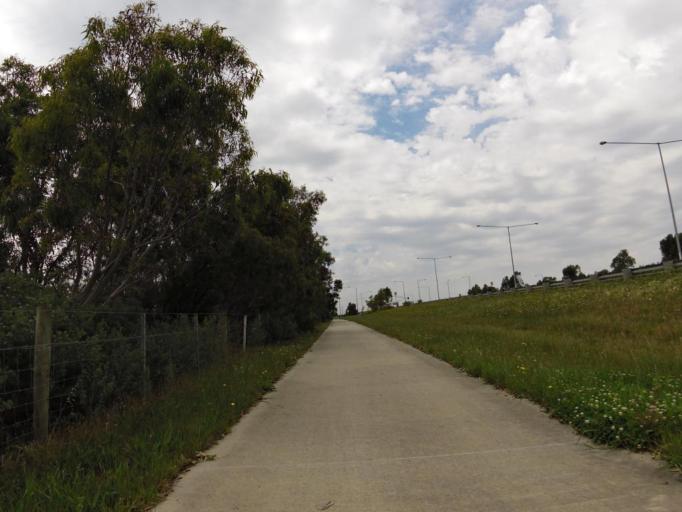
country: AU
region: Victoria
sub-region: Greater Dandenong
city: Keysborough
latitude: -38.0006
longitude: 145.1883
